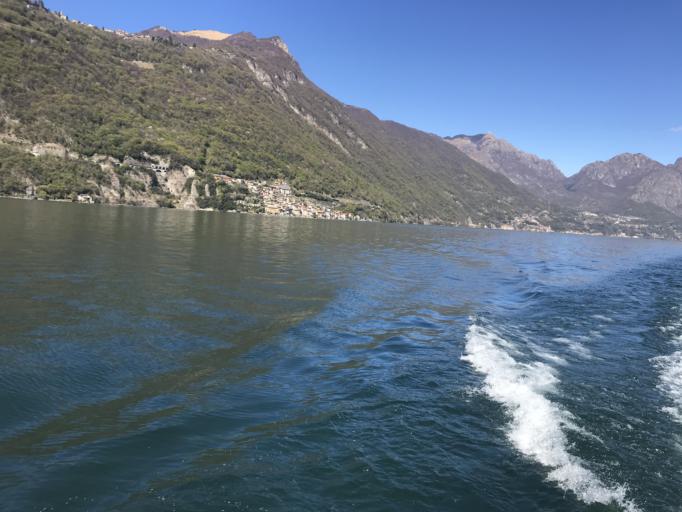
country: IT
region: Lombardy
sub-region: Provincia di Como
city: Lanzo d'Intelvi
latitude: 45.9940
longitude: 8.9963
